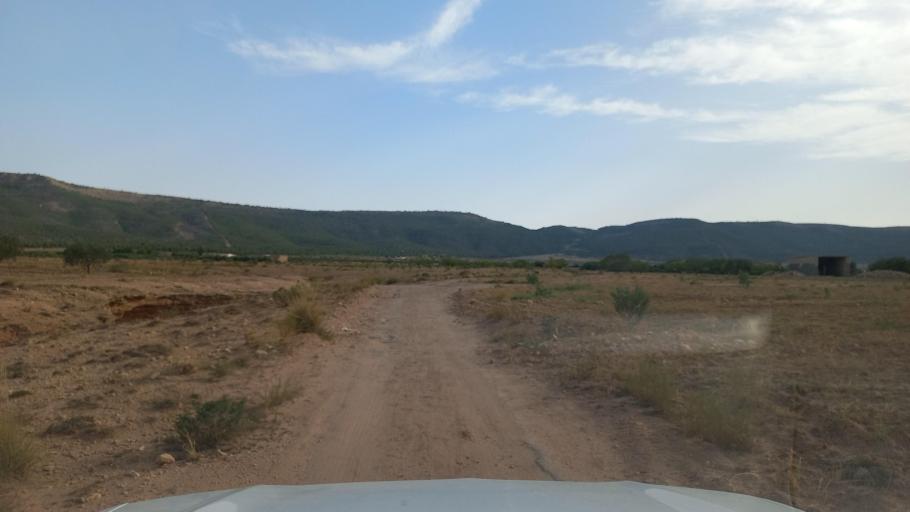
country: TN
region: Al Qasrayn
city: Kasserine
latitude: 35.3557
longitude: 8.8540
